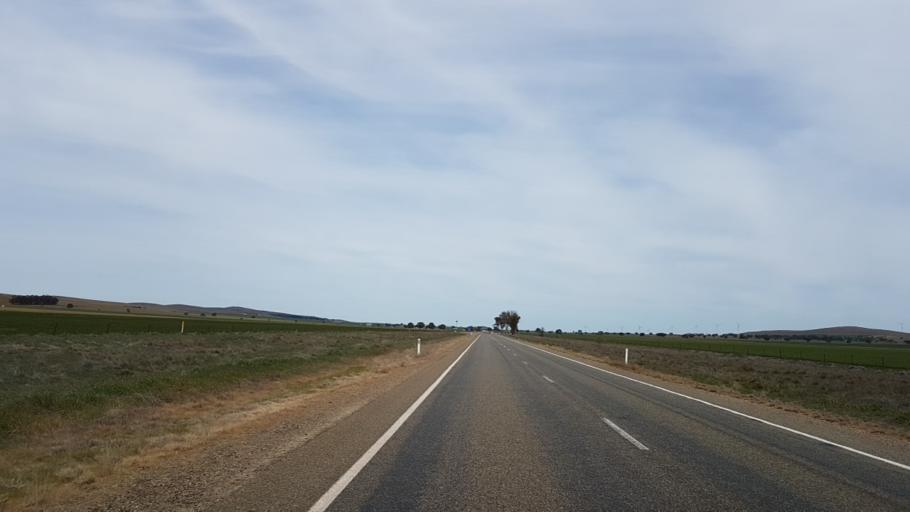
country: AU
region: South Australia
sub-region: Northern Areas
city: Jamestown
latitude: -33.0524
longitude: 138.6180
